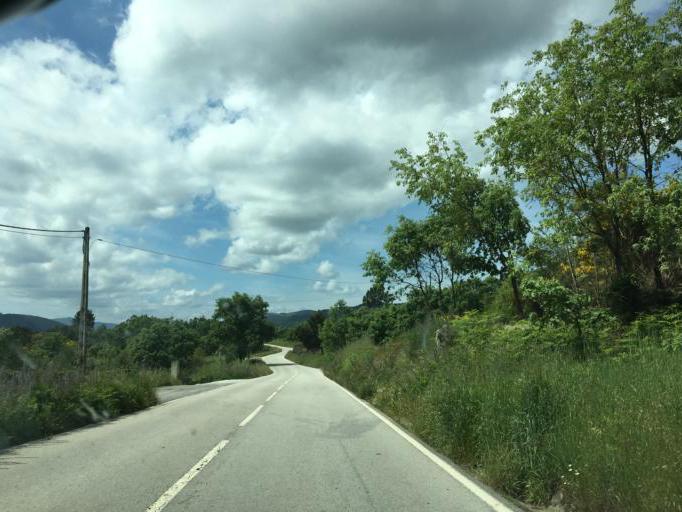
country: PT
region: Vila Real
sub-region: Boticas
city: Boticas
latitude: 41.7029
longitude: -7.6434
